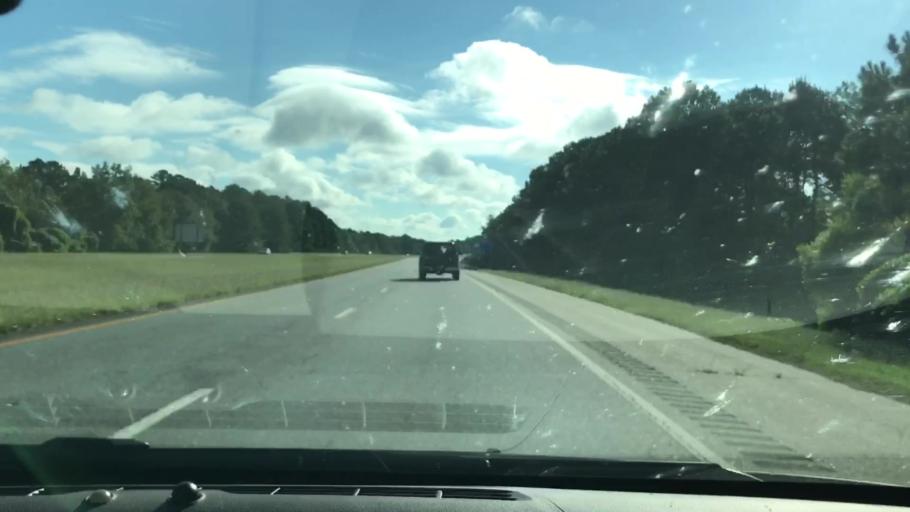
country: US
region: Georgia
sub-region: Dougherty County
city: Albany
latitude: 31.6152
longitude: -84.1917
